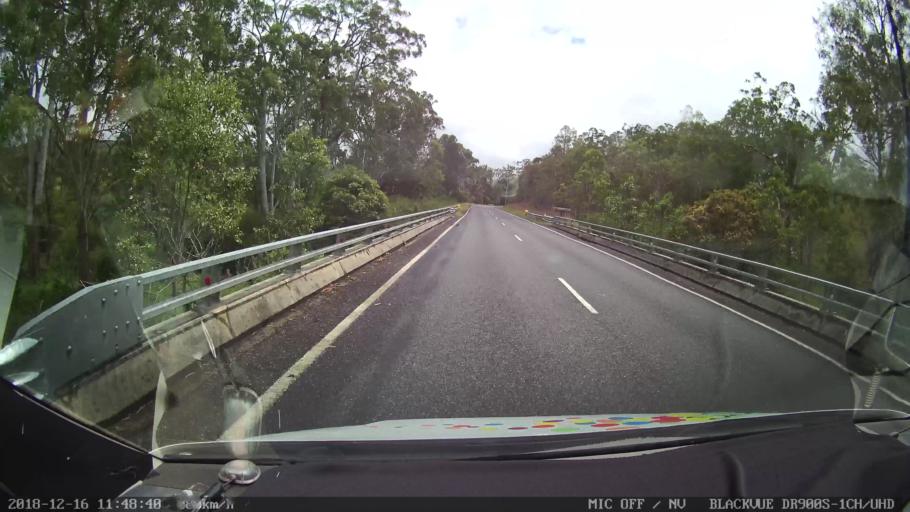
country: AU
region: New South Wales
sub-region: Tenterfield Municipality
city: Carrolls Creek
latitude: -28.9201
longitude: 152.2494
